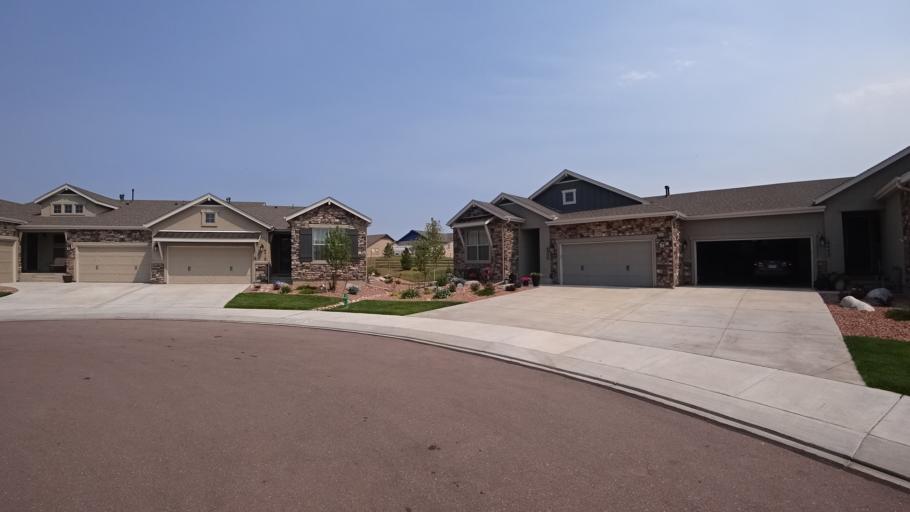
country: US
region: Colorado
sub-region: El Paso County
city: Black Forest
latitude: 38.9684
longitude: -104.7138
